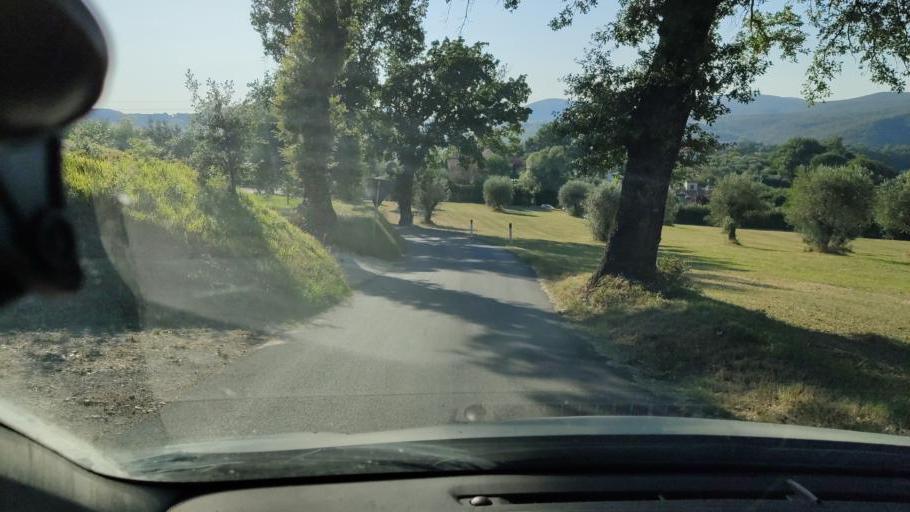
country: IT
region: Umbria
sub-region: Provincia di Terni
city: Amelia
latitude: 42.5399
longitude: 12.4046
